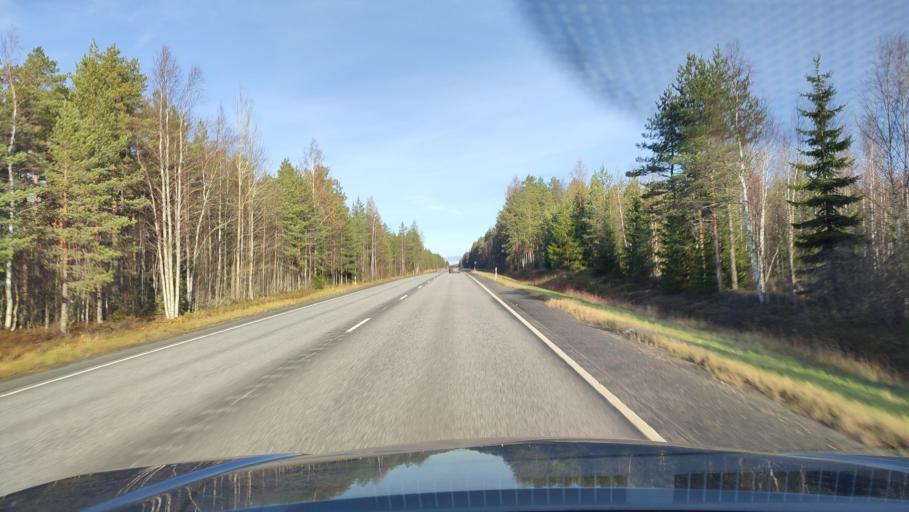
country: FI
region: Ostrobothnia
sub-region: Vaasa
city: Malax
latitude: 62.7930
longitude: 21.6718
